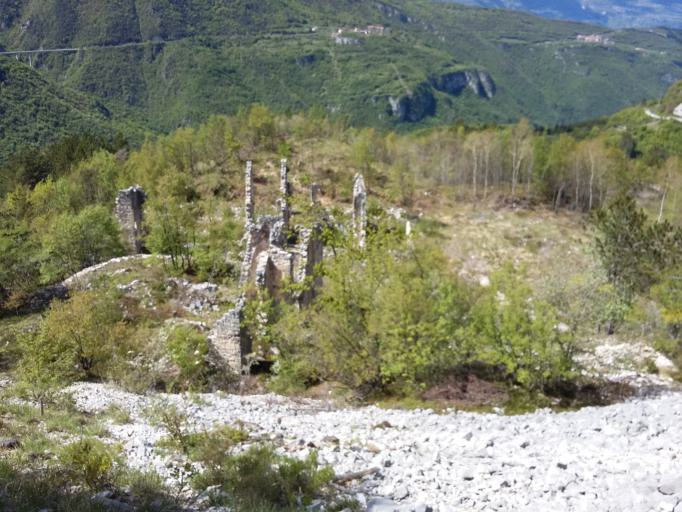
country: IT
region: Trentino-Alto Adige
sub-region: Provincia di Trento
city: Moscheri
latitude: 45.8275
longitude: 11.0874
